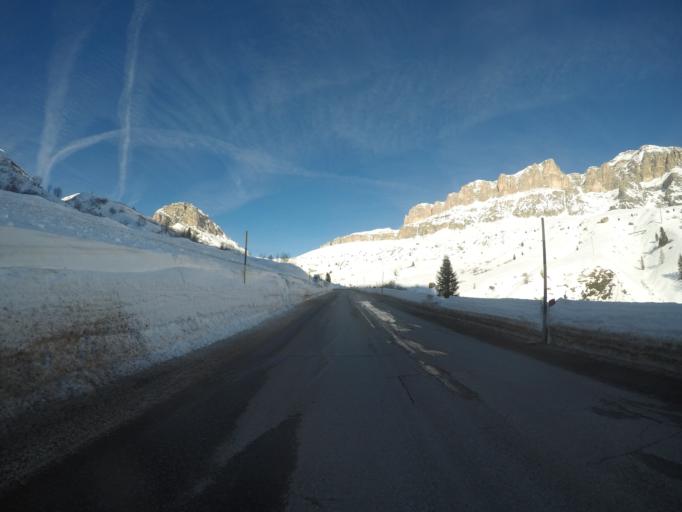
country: IT
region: Trentino-Alto Adige
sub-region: Provincia di Trento
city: Canazei
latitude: 46.4836
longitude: 11.8346
